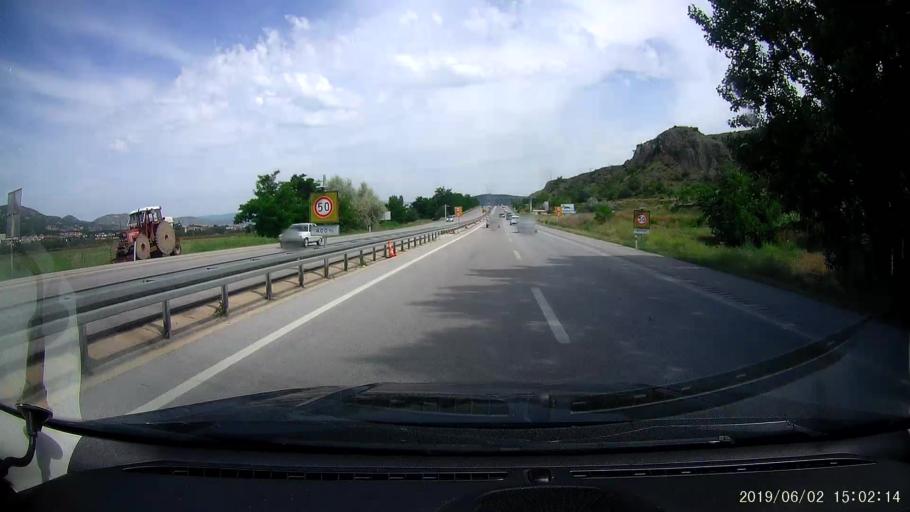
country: TR
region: Corum
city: Osmancik
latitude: 40.9829
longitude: 34.7640
